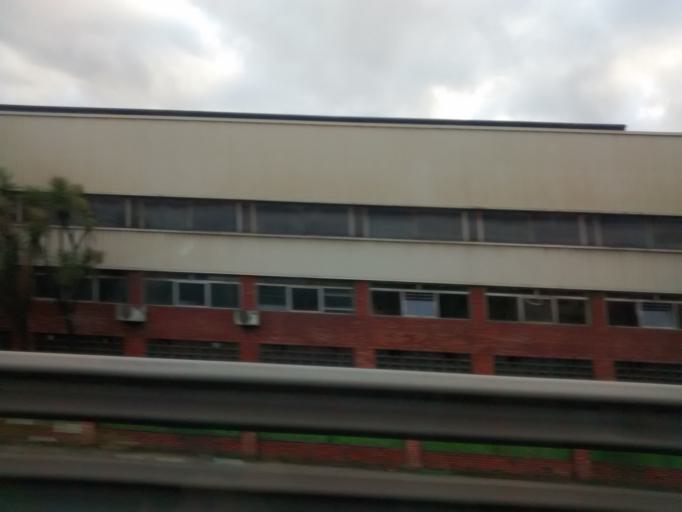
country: ES
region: Cantabria
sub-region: Provincia de Cantabria
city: El Astillero
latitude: 43.4144
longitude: -3.8379
